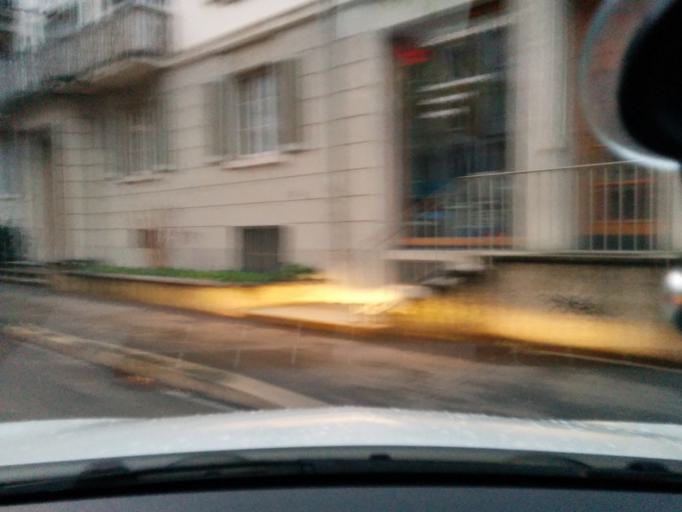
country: CH
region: Zurich
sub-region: Bezirk Zuerich
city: Zuerich (Kreis 3) / Sihlfeld
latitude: 47.3772
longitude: 8.5129
